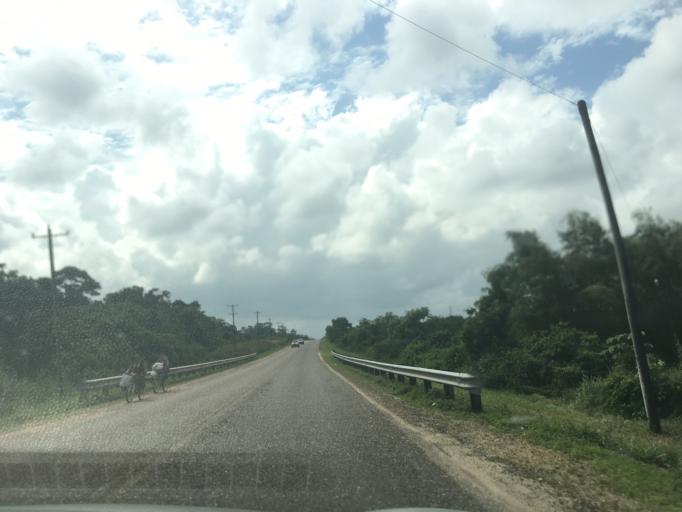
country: BZ
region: Stann Creek
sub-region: Dangriga
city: Dangriga
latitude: 16.9730
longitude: -88.3016
